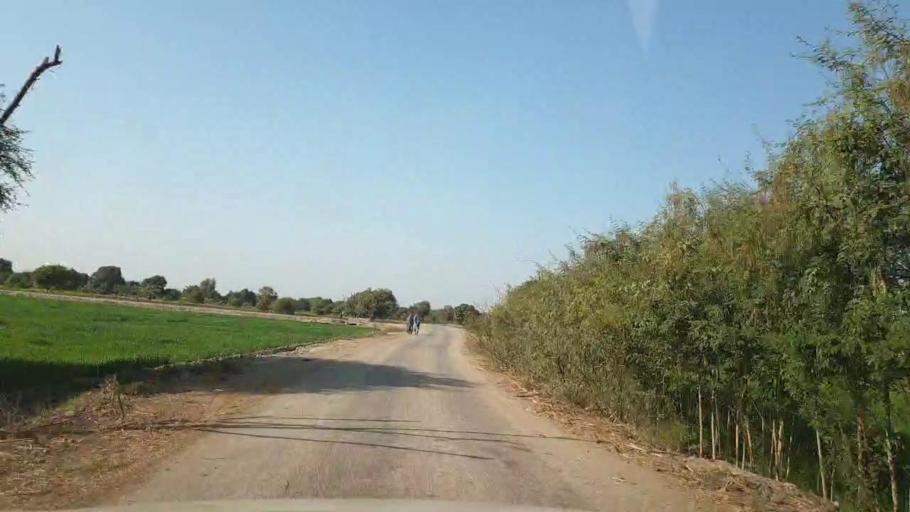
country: PK
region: Sindh
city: Tando Allahyar
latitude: 25.4946
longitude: 68.6535
